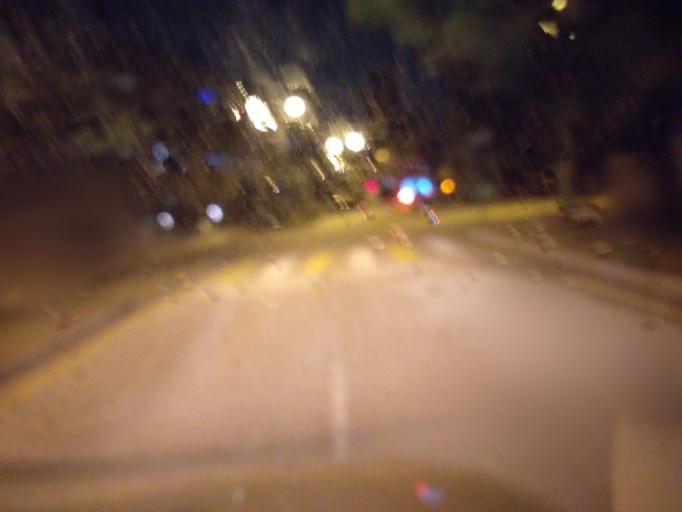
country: TR
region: Ankara
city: Batikent
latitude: 39.8792
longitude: 32.7131
